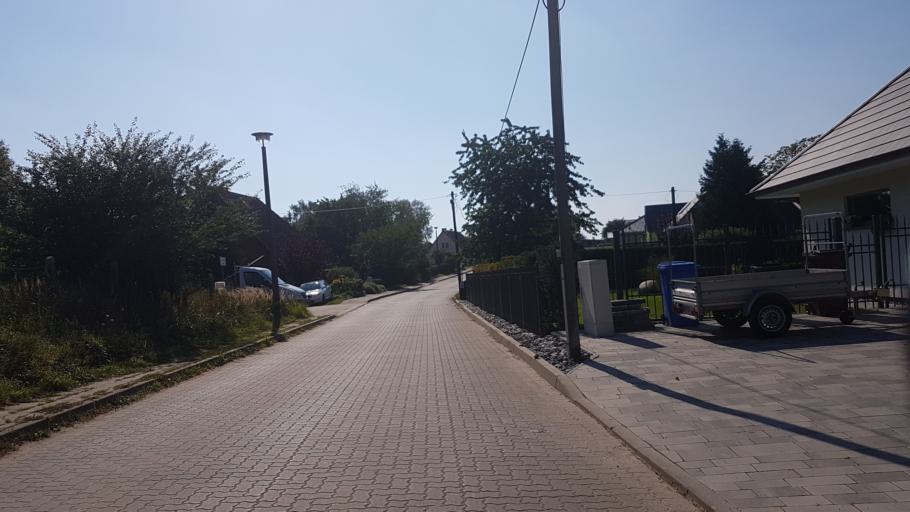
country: DE
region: Mecklenburg-Vorpommern
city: Putbus
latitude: 54.3553
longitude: 13.5138
